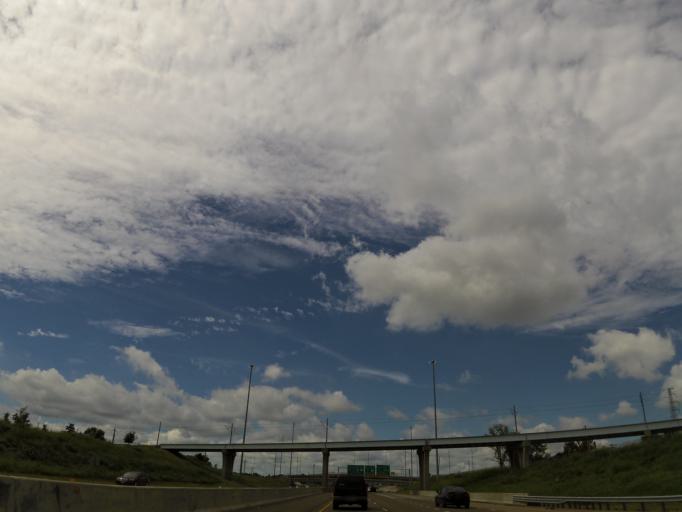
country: US
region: Illinois
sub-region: Saint Clair County
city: East Saint Louis
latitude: 38.6290
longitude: -90.1397
